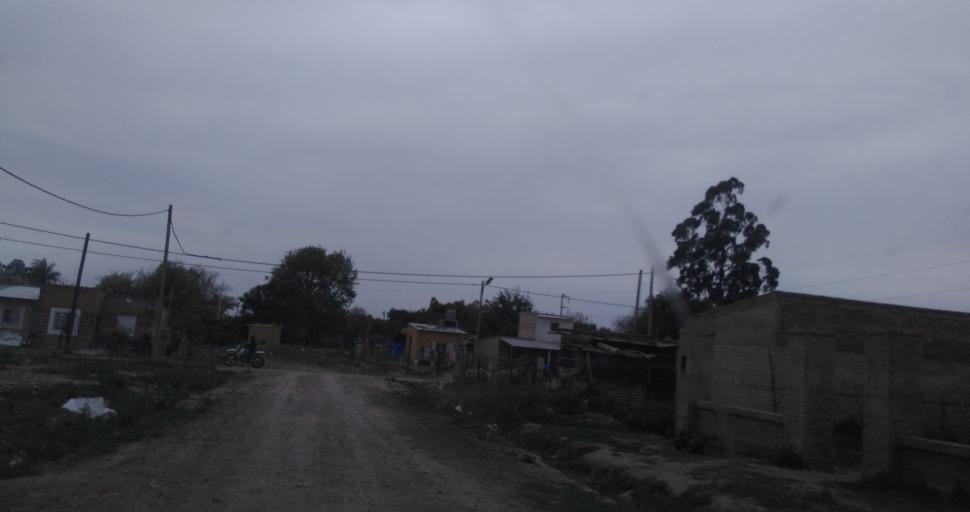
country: AR
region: Chaco
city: Fontana
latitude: -27.4185
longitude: -59.0220
